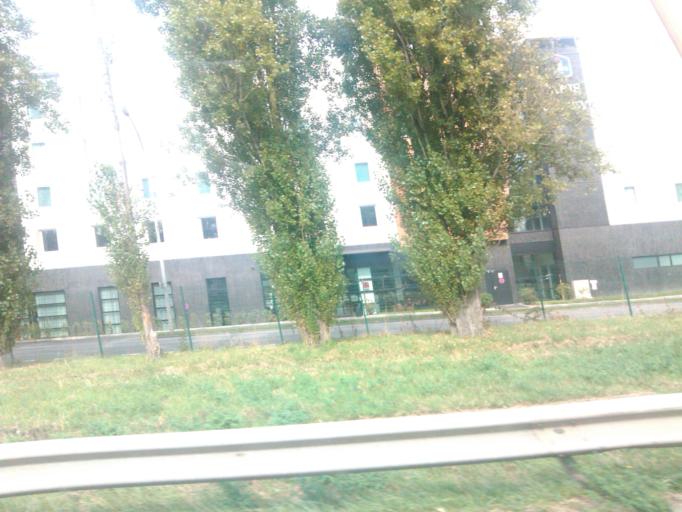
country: FR
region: Ile-de-France
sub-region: Departement des Yvelines
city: Velizy-Villacoublay
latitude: 48.7790
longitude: 2.2036
